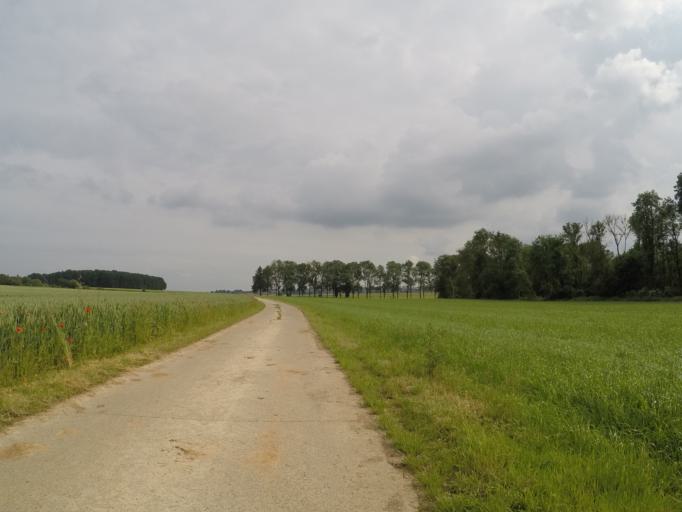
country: BE
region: Wallonia
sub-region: Province de Namur
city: Assesse
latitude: 50.3265
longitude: 5.0506
